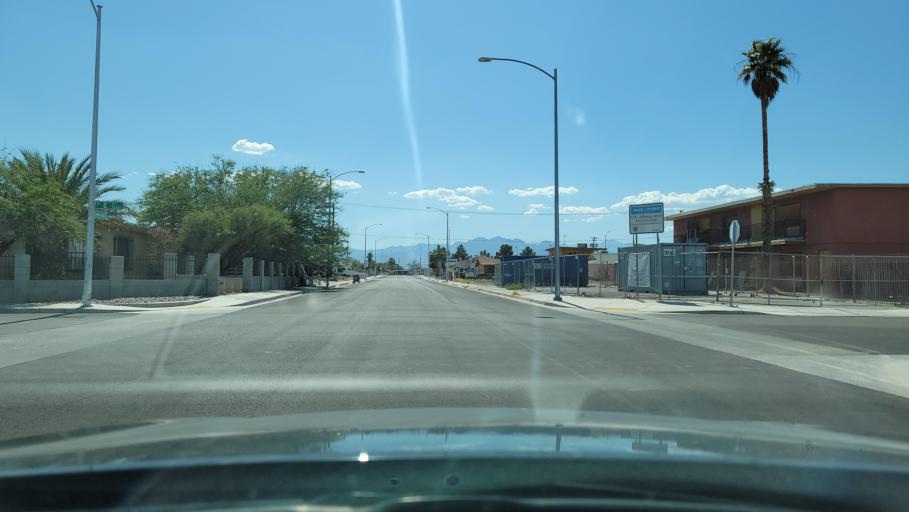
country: US
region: Nevada
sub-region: Clark County
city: Las Vegas
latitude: 36.1829
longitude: -115.1481
